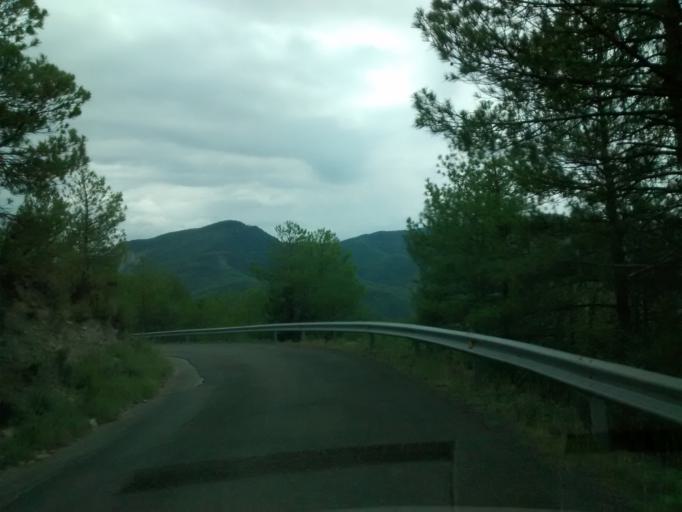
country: ES
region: Aragon
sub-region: Provincia de Huesca
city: Laspuna
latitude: 42.5178
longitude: 0.1309
